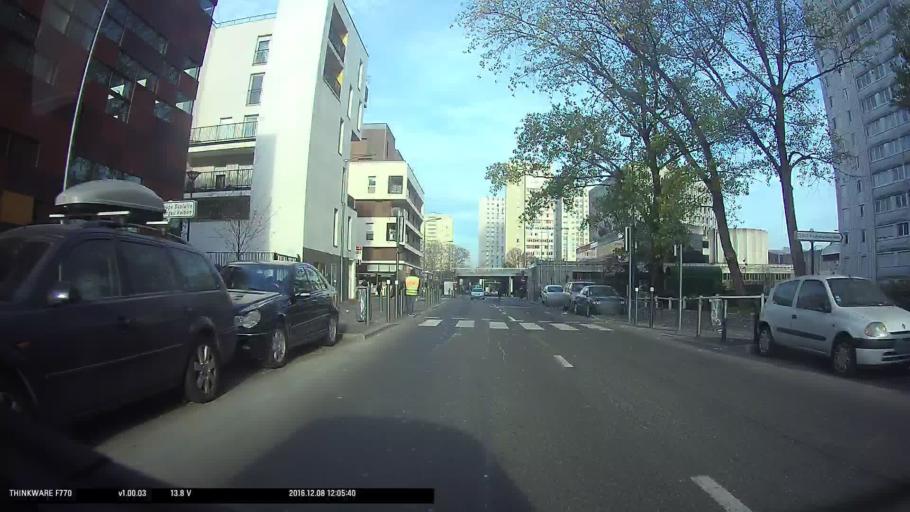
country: FR
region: Ile-de-France
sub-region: Departement de Seine-Saint-Denis
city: Bobigny
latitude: 48.9049
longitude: 2.4444
